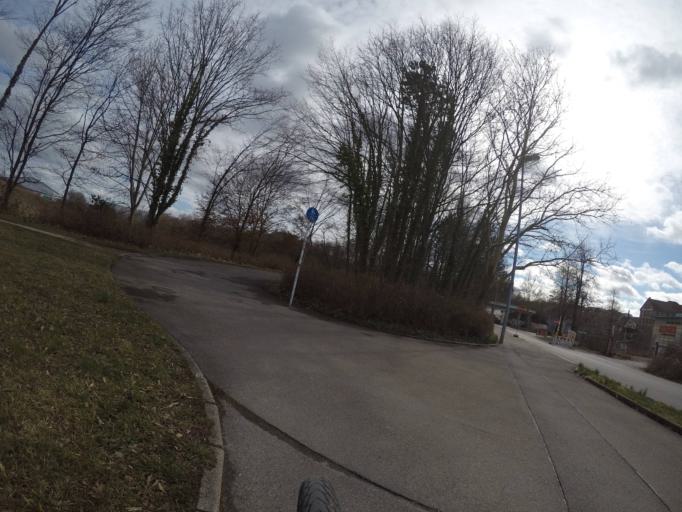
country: DE
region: Baden-Wuerttemberg
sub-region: Tuebingen Region
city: Reutlingen
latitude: 48.5023
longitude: 9.2015
